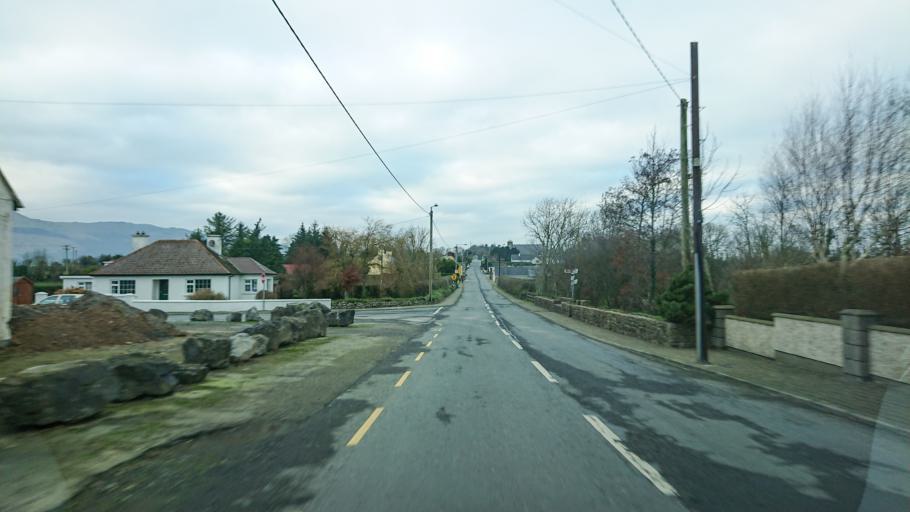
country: IE
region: Munster
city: Carrick-on-Suir
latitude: 52.3044
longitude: -7.4928
